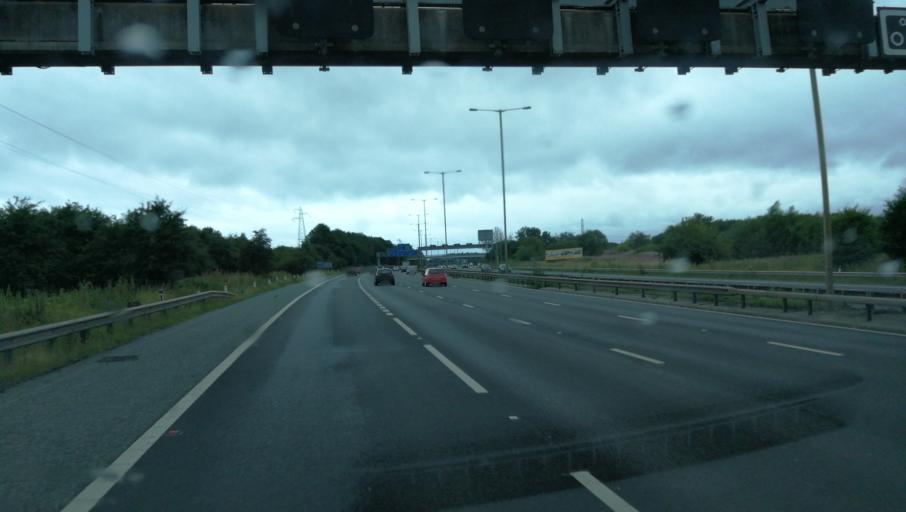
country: GB
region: England
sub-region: Manchester
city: Swinton
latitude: 53.5250
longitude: -2.3429
